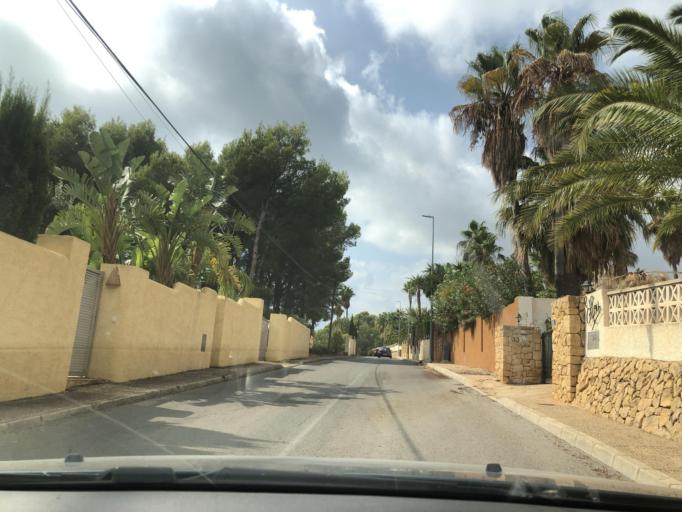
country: ES
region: Valencia
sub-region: Provincia de Alicante
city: Altea
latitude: 38.6357
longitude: -0.0670
